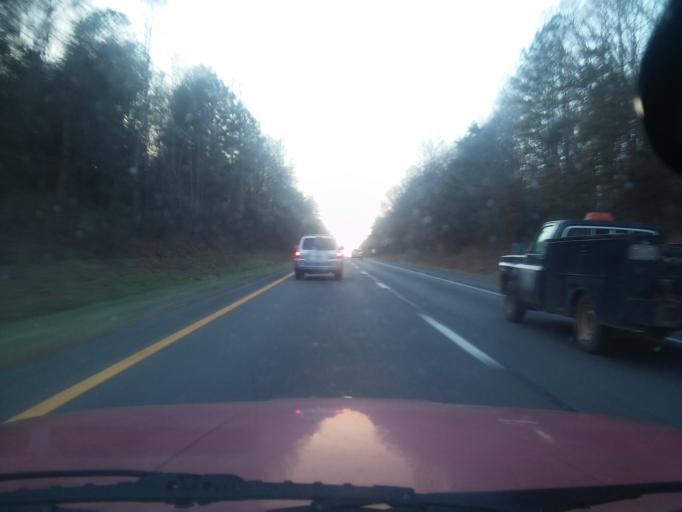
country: US
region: Virginia
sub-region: Goochland County
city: Goochland
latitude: 37.7128
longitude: -77.7917
